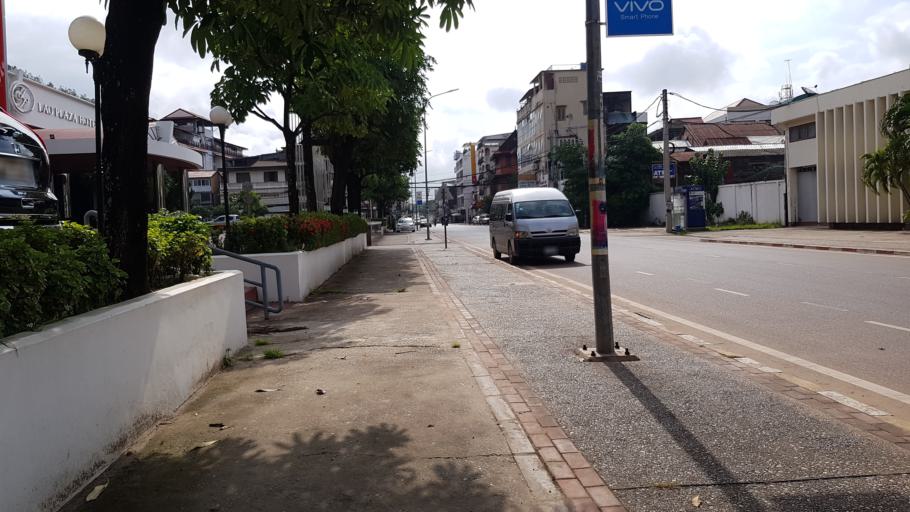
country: LA
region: Vientiane
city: Vientiane
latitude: 17.9665
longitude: 102.6080
